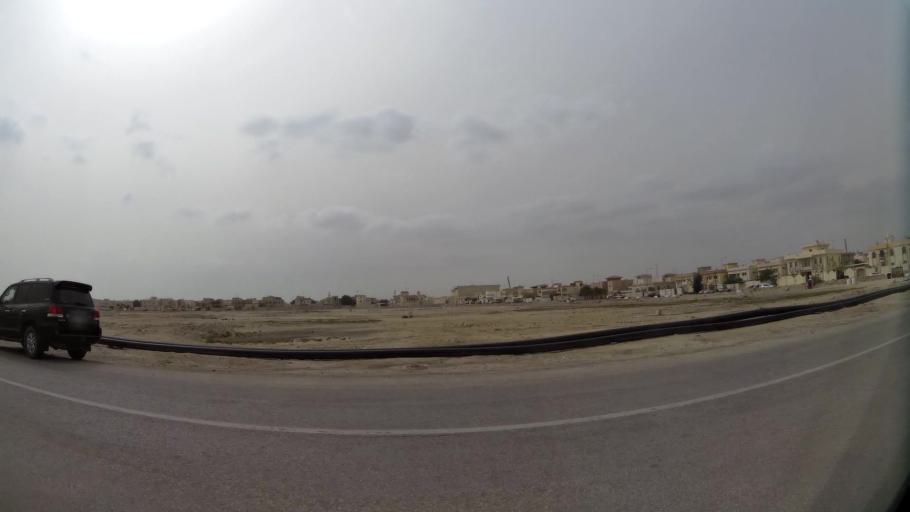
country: QA
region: Baladiyat ad Dawhah
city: Doha
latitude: 25.2452
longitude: 51.5300
